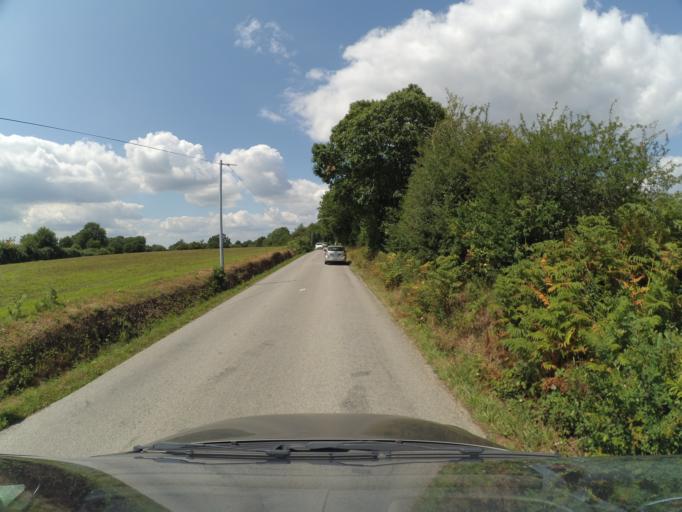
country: FR
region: Brittany
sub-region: Departement du Morbihan
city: Landaul
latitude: 47.7339
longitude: -3.0463
